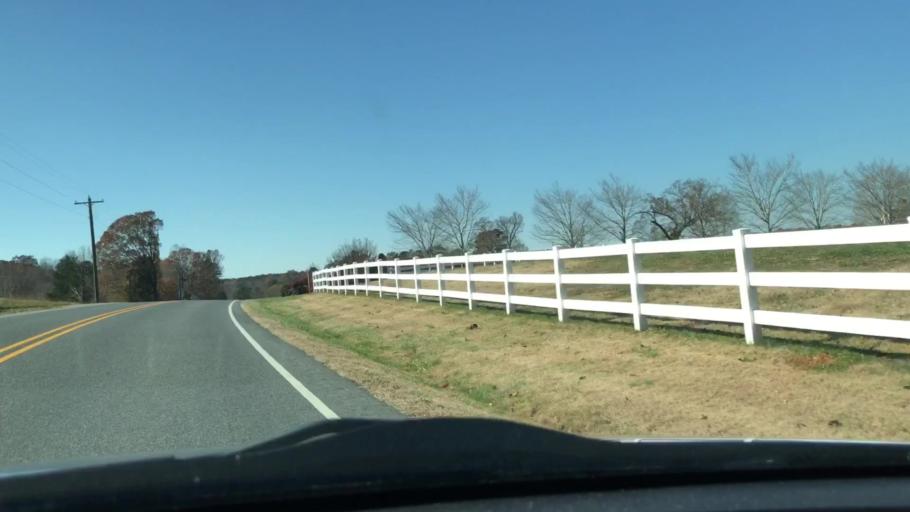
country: US
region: North Carolina
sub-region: Randolph County
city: Asheboro
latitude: 35.6742
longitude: -79.9394
